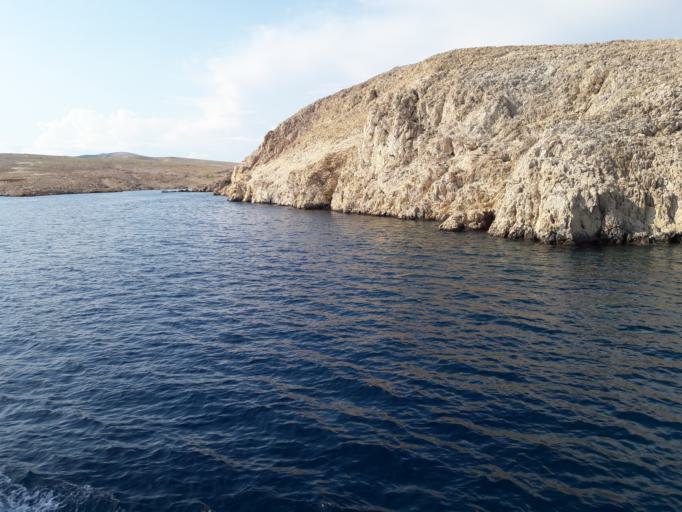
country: HR
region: Primorsko-Goranska
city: Banjol
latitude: 44.7041
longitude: 14.8668
